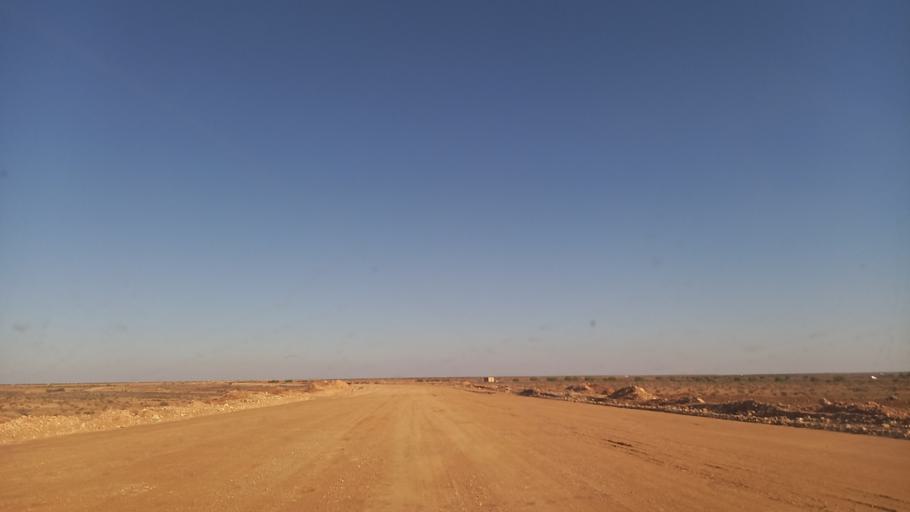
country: TN
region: Tataouine
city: Tataouine
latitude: 33.1329
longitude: 10.5030
